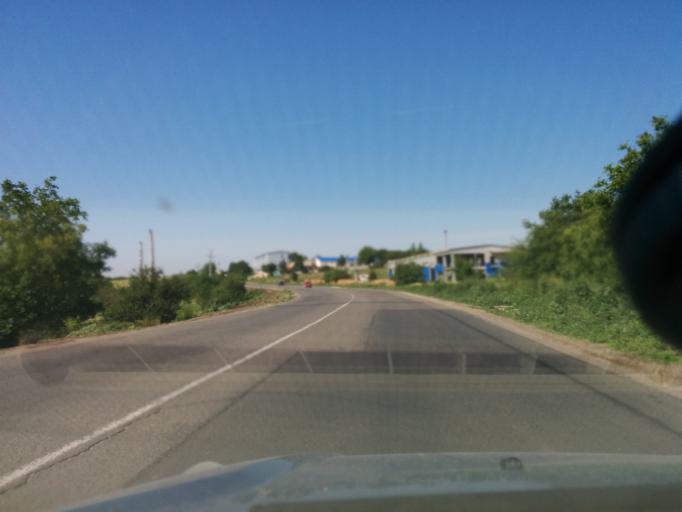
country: MD
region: Chisinau
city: Stauceni
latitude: 47.0457
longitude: 28.9100
